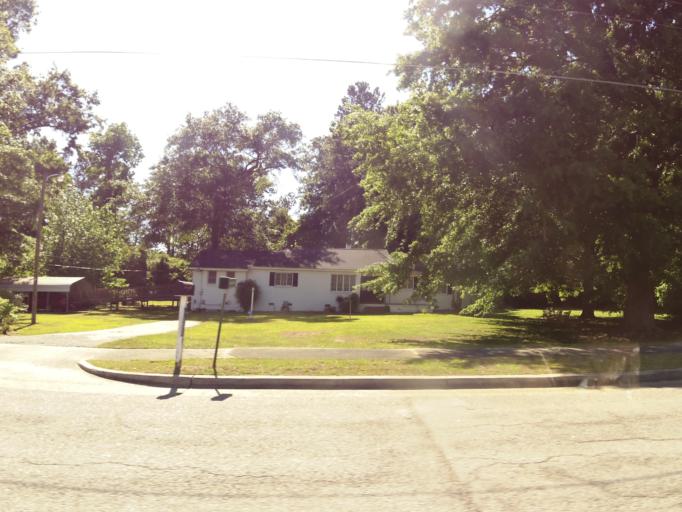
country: US
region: South Carolina
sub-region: Bamberg County
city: Denmark
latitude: 33.2991
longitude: -81.1458
